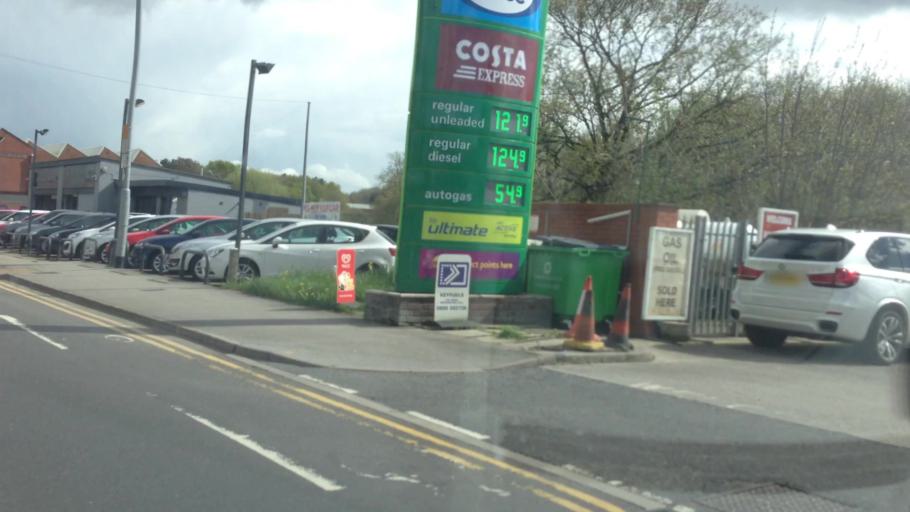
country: GB
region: England
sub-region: City and Borough of Leeds
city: Leeds
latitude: 53.8088
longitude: -1.5897
